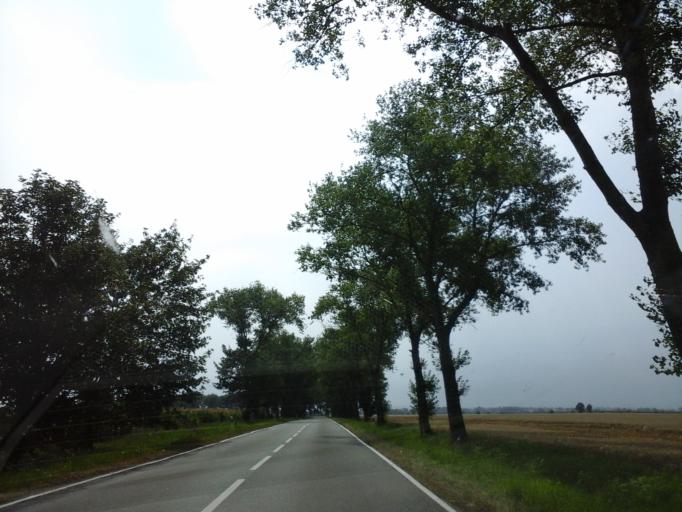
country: PL
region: Lower Silesian Voivodeship
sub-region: Powiat strzelinski
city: Strzelin
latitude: 50.8586
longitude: 17.0643
